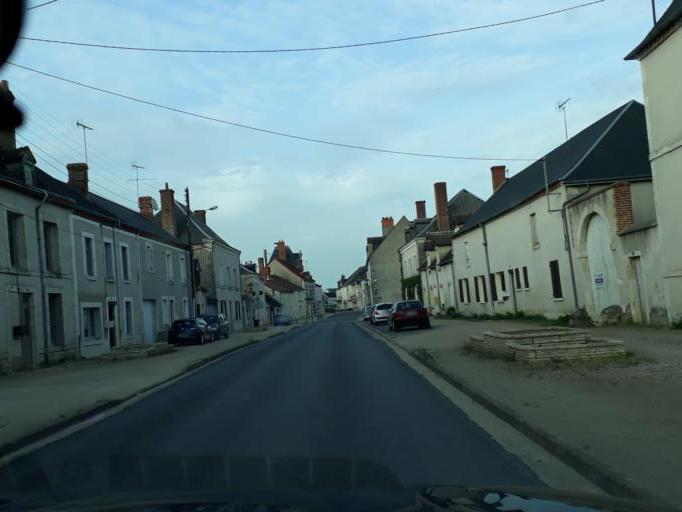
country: FR
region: Centre
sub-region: Departement du Loir-et-Cher
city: Saint-Laurent-Nouan
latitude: 47.7160
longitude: 1.6098
